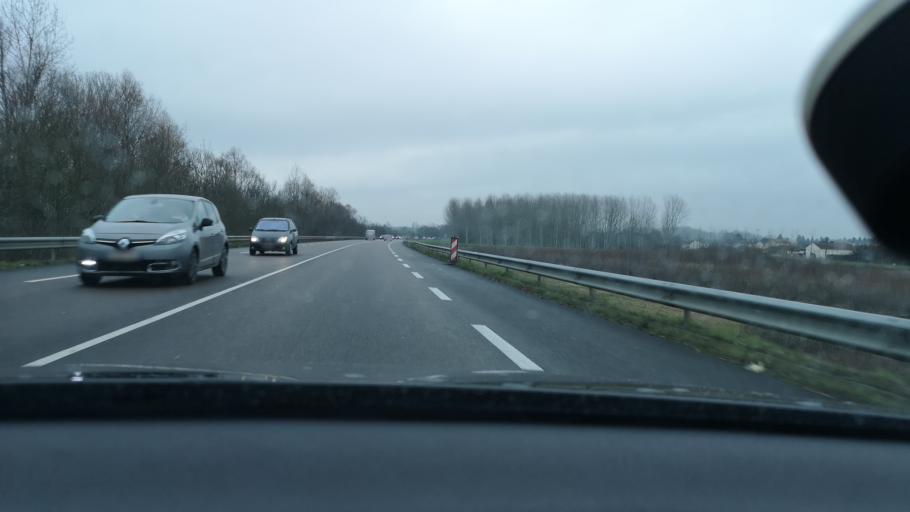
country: FR
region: Bourgogne
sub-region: Departement de Saone-et-Loire
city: Saint-Marcel
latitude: 46.7859
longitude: 4.8921
